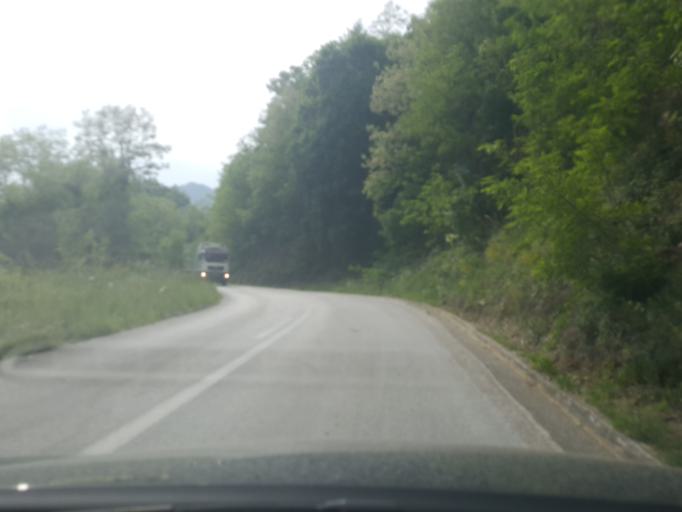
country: RS
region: Central Serbia
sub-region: Zlatiborski Okrug
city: Bajina Basta
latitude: 44.0415
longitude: 19.6276
